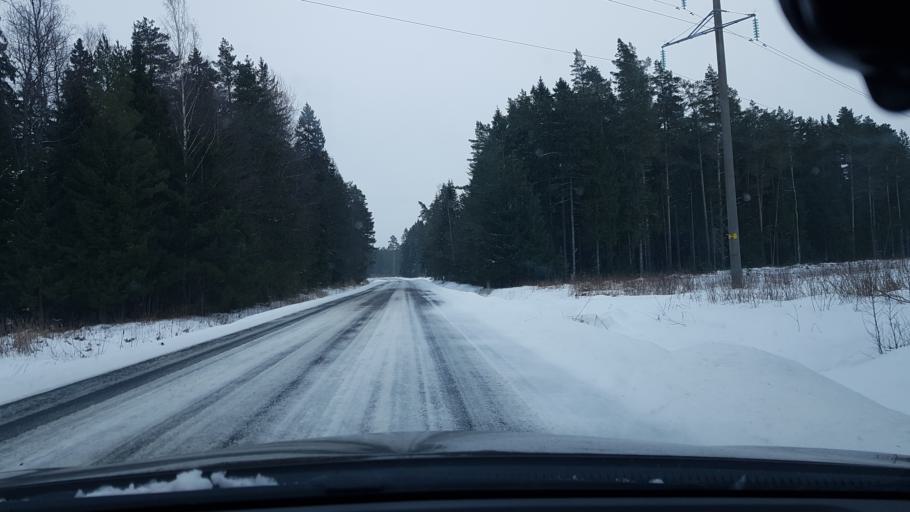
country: EE
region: Harju
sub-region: Loksa linn
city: Loksa
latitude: 59.5523
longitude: 25.7953
